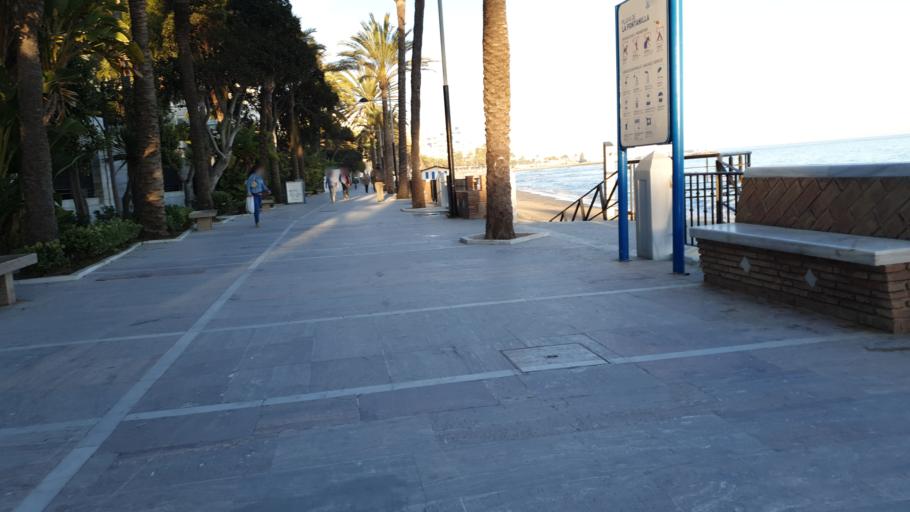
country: ES
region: Andalusia
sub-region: Provincia de Malaga
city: Marbella
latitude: 36.5067
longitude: -4.9006
